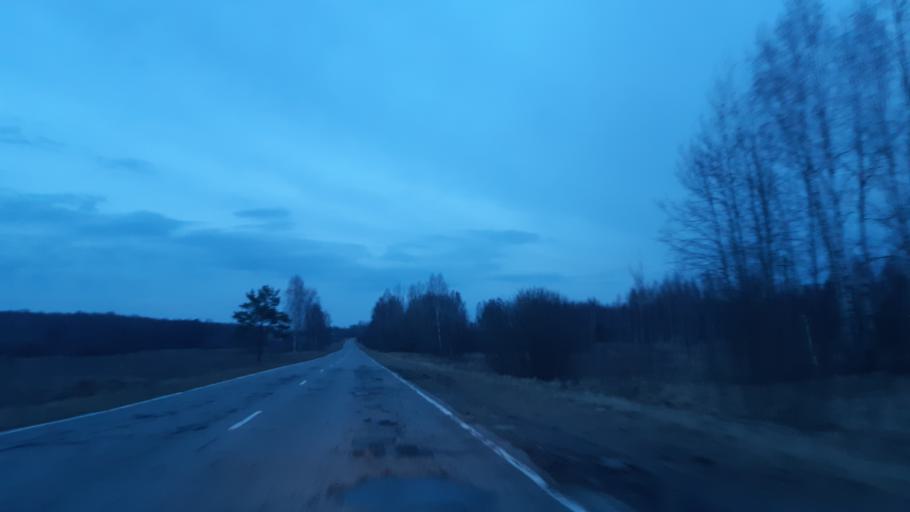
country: RU
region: Vladimir
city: Luknovo
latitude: 56.1811
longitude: 42.0119
